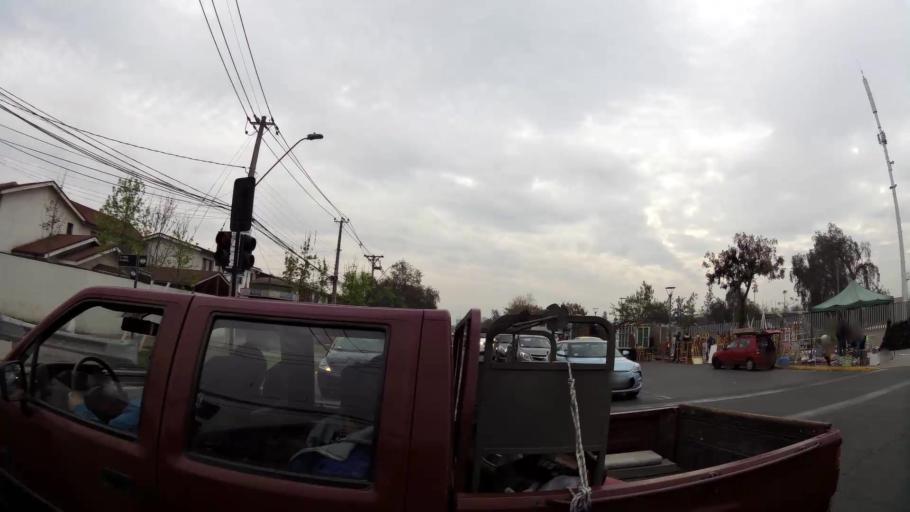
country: CL
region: Santiago Metropolitan
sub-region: Provincia de Santiago
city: Villa Presidente Frei, Nunoa, Santiago, Chile
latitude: -33.4703
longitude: -70.6066
